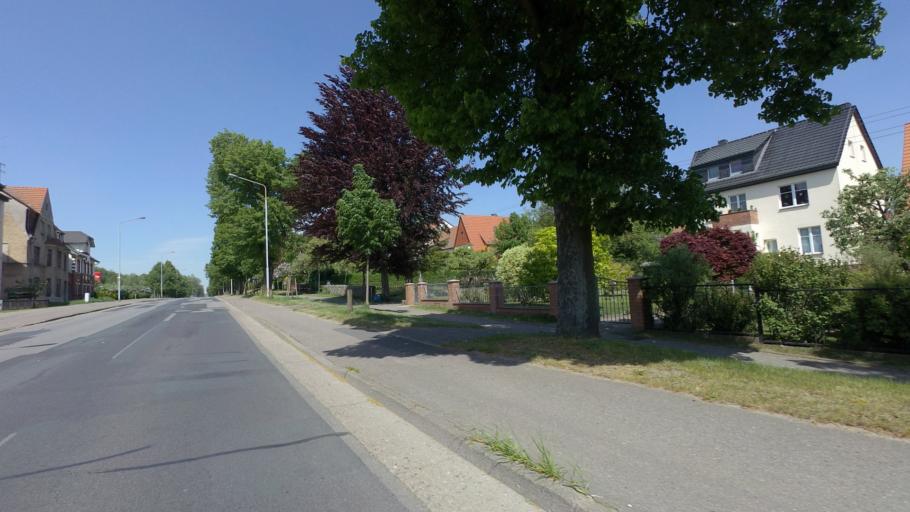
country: DE
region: Mecklenburg-Vorpommern
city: Neustrelitz
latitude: 53.3371
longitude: 13.0890
